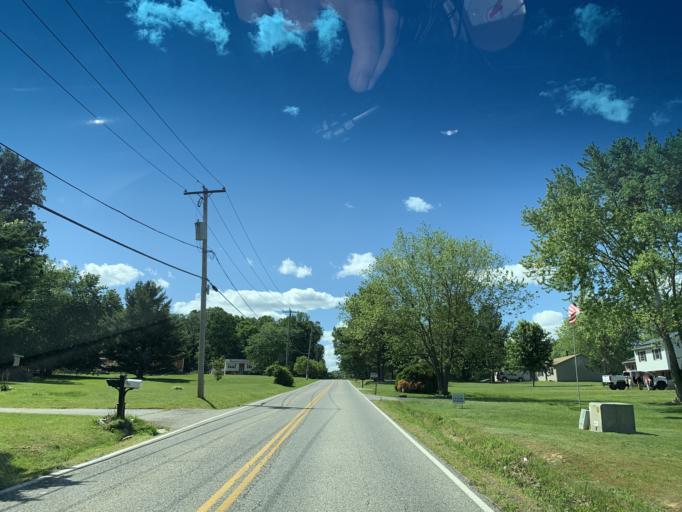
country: US
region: Maryland
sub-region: Cecil County
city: North East
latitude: 39.5610
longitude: -75.8852
